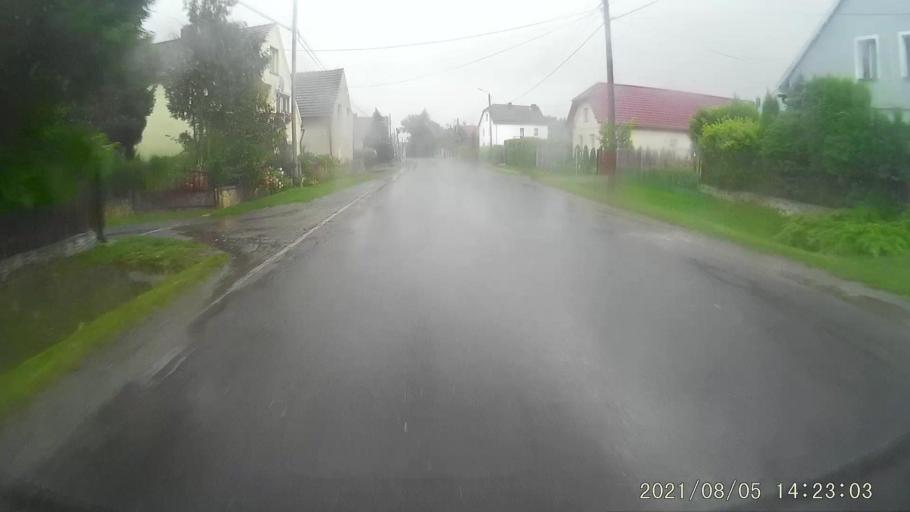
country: PL
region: Opole Voivodeship
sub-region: Powiat nyski
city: Korfantow
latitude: 50.4800
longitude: 17.6506
